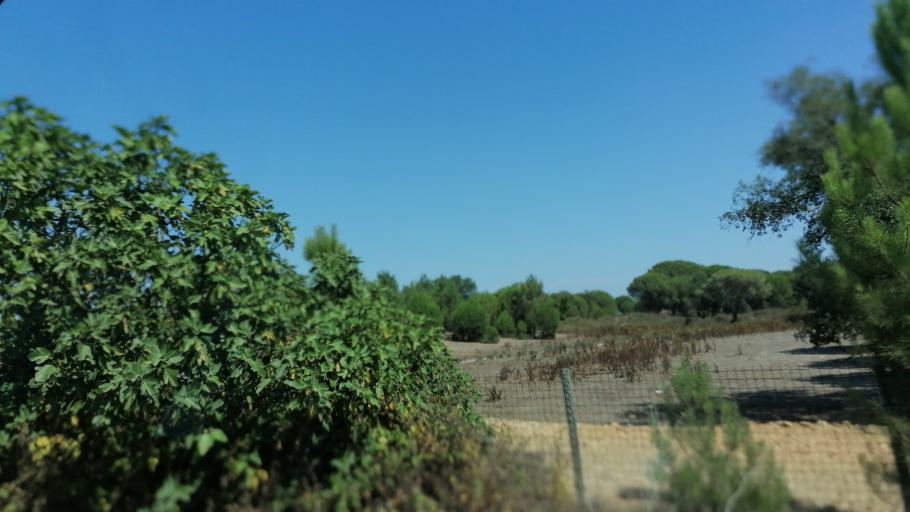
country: PT
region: Santarem
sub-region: Benavente
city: Poceirao
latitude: 38.7278
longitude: -8.7039
